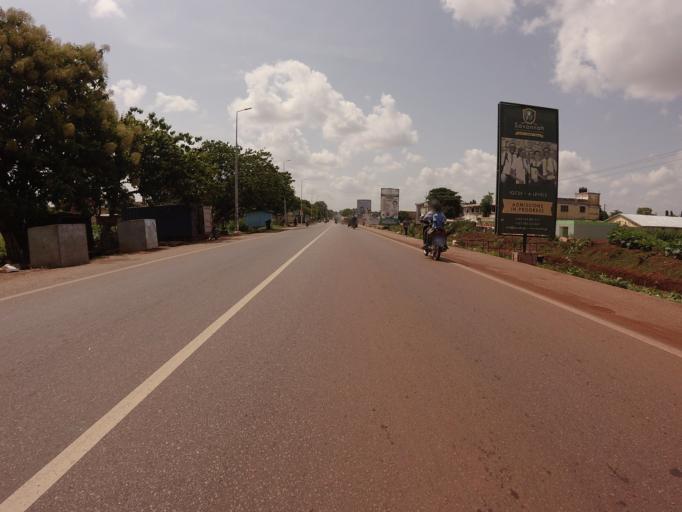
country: GH
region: Northern
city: Tamale
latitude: 9.4421
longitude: -0.8440
